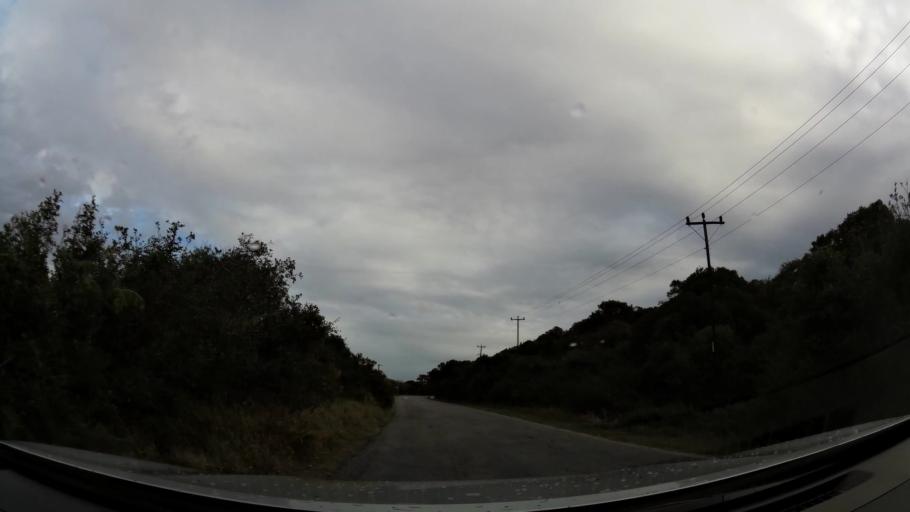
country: ZA
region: Eastern Cape
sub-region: Nelson Mandela Bay Metropolitan Municipality
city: Port Elizabeth
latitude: -34.0099
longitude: 25.4943
